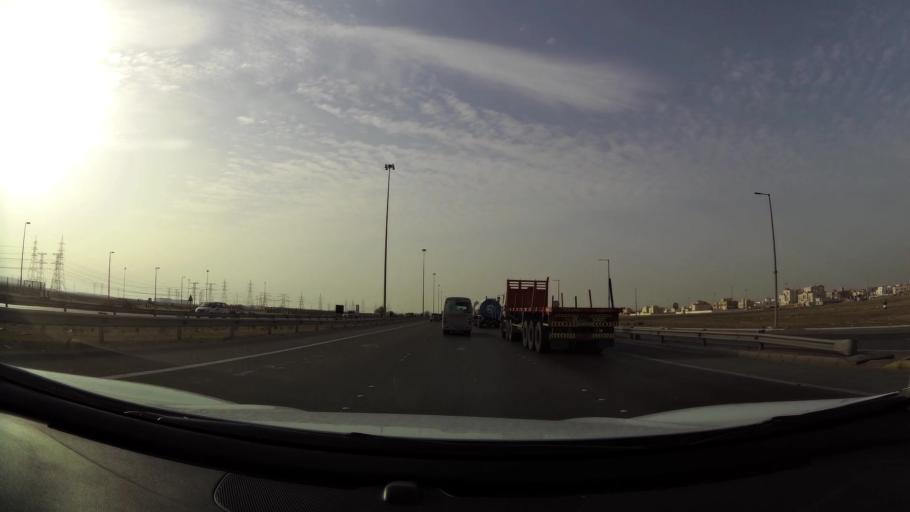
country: AE
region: Abu Dhabi
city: Abu Dhabi
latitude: 24.3029
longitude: 54.5361
